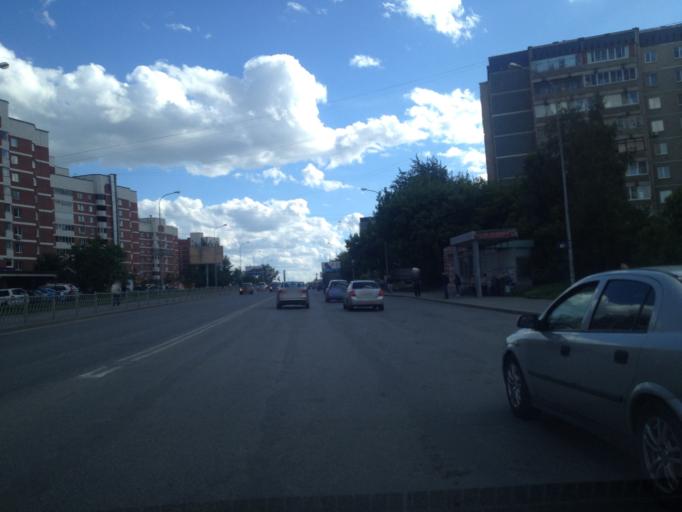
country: RU
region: Sverdlovsk
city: Yekaterinburg
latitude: 56.8519
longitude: 60.5702
